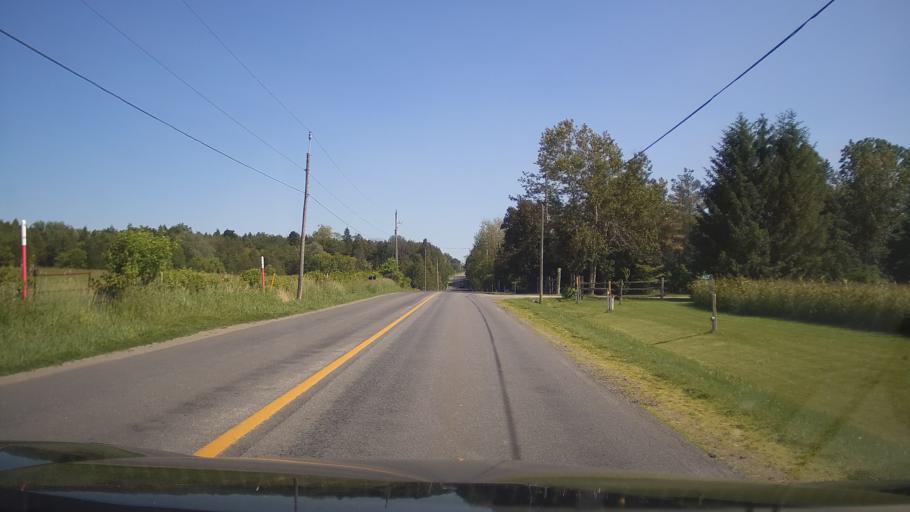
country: CA
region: Ontario
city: Oshawa
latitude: 43.9610
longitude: -78.7325
